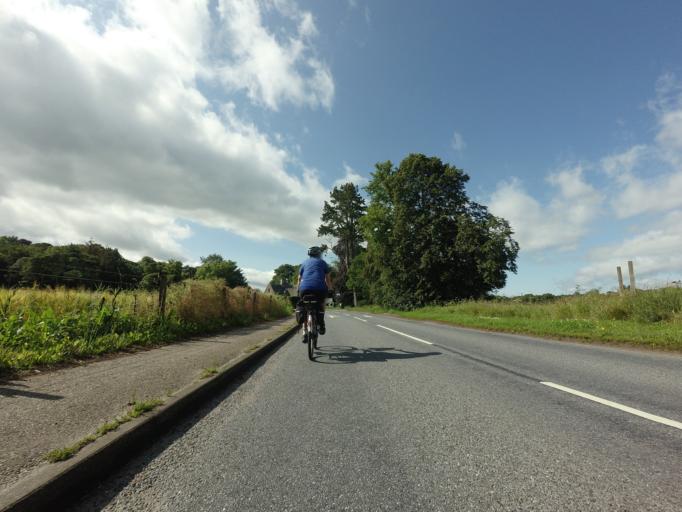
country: GB
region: Scotland
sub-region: Highland
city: Nairn
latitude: 57.5767
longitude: -3.8613
